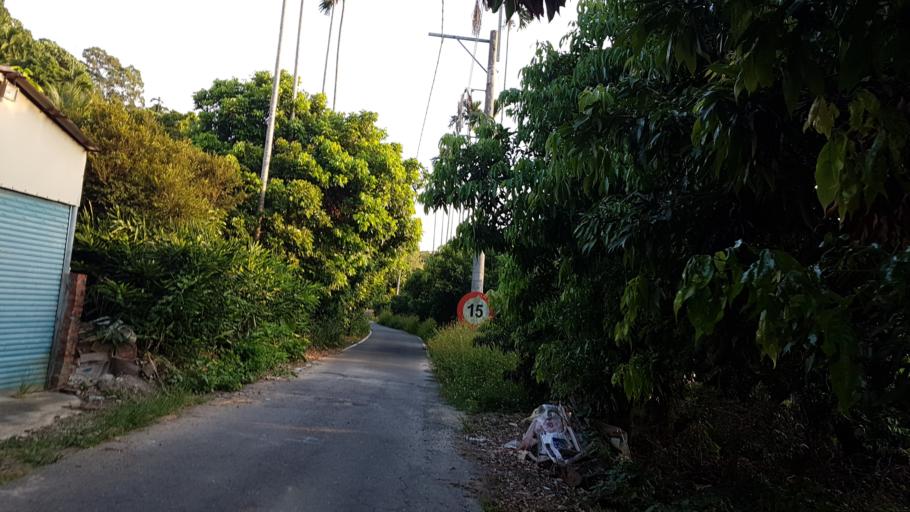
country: TW
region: Taiwan
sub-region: Chiayi
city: Jiayi Shi
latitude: 23.3657
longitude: 120.4643
